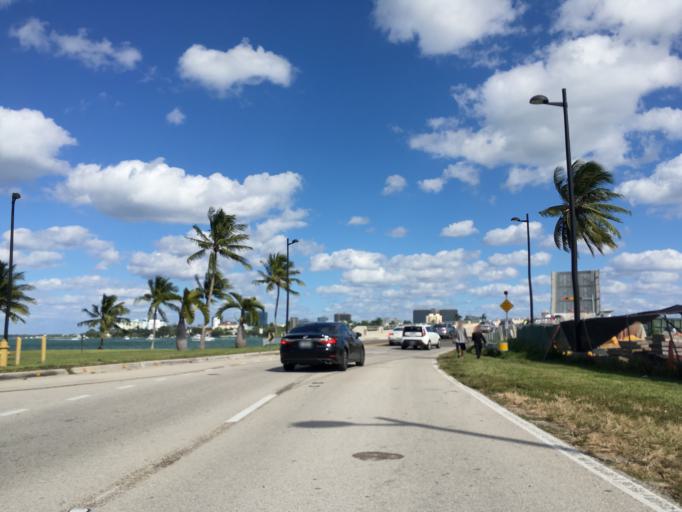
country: US
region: Florida
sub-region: Miami-Dade County
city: Bay Harbor Islands
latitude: 25.8876
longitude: -80.1446
